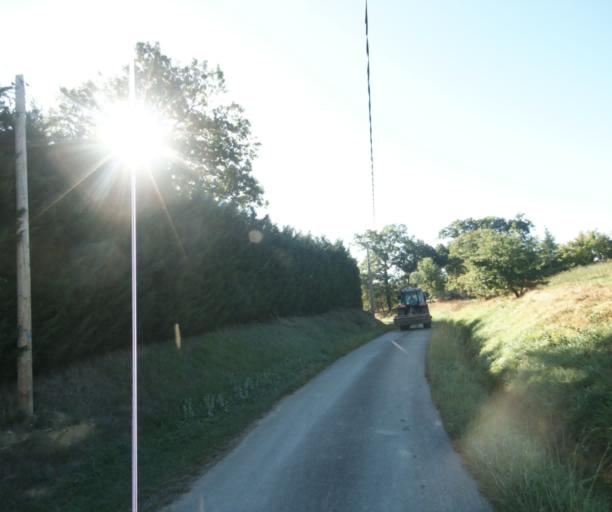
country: FR
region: Midi-Pyrenees
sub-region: Departement du Gers
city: Gondrin
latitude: 43.8363
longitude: 0.2808
